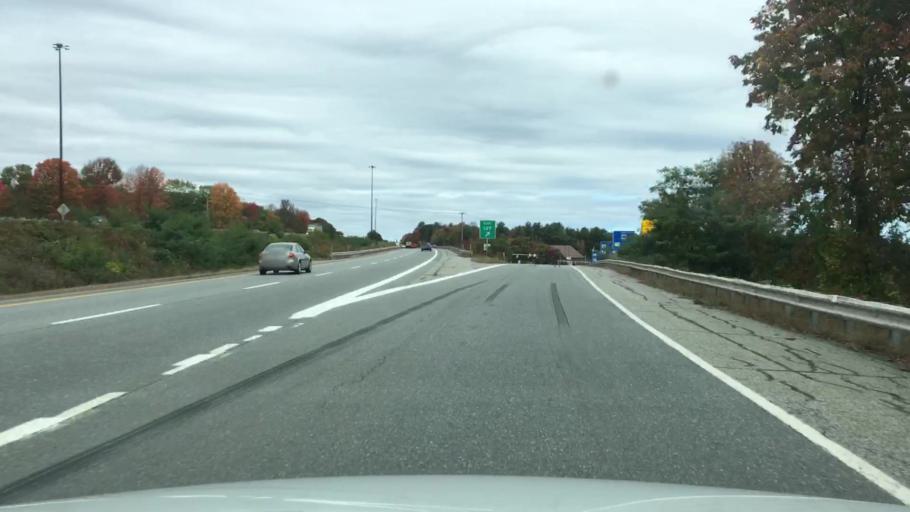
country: US
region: Maine
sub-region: Kennebec County
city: Oakland
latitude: 44.5428
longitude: -69.6809
